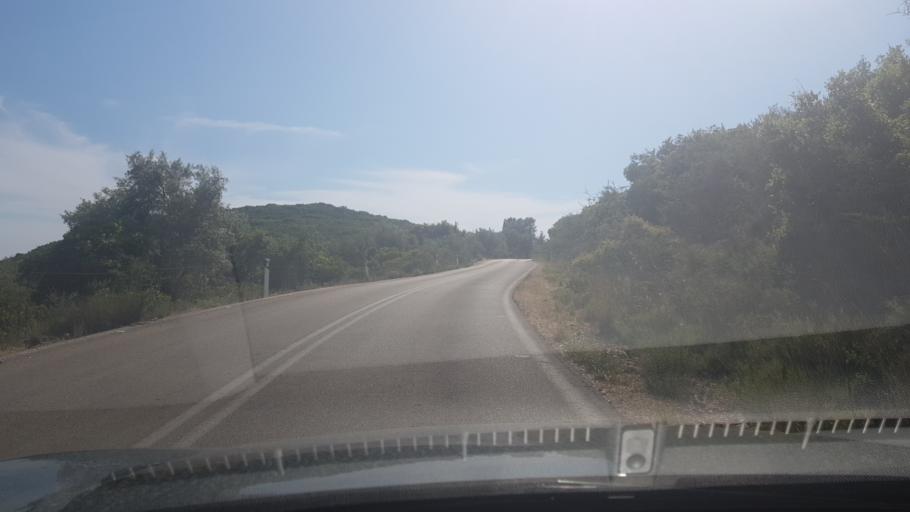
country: GR
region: Ionian Islands
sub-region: Lefkada
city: Nidri
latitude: 38.6529
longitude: 20.6738
